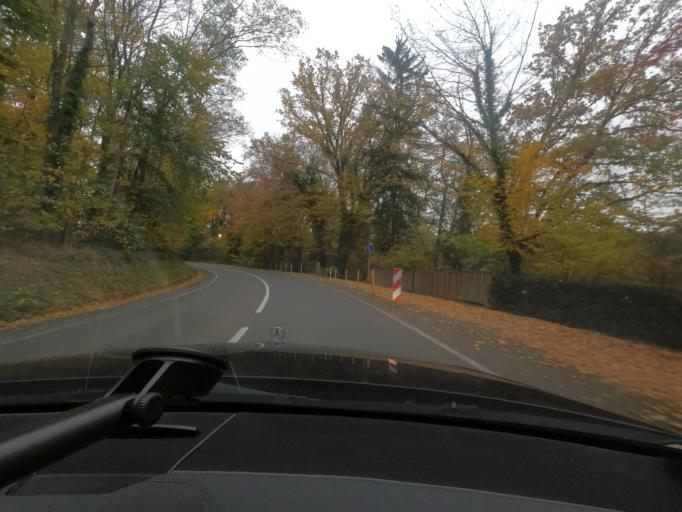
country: DE
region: North Rhine-Westphalia
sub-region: Regierungsbezirk Arnsberg
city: Mohnesee
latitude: 51.4793
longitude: 8.1787
